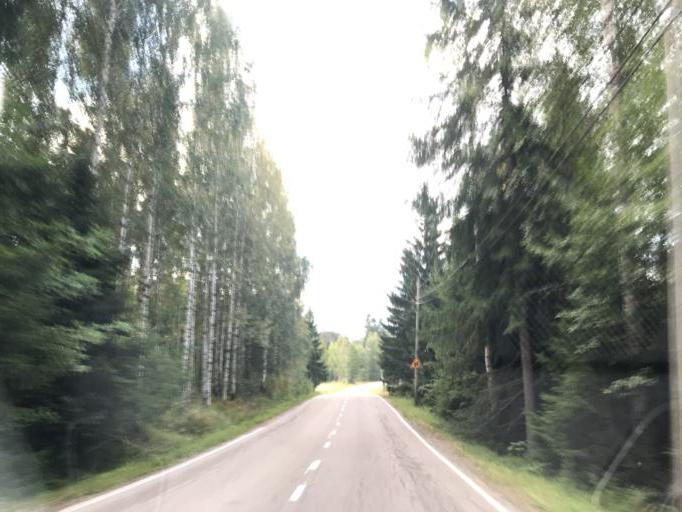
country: FI
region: Uusimaa
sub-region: Helsinki
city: Vihti
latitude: 60.3902
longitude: 24.5173
